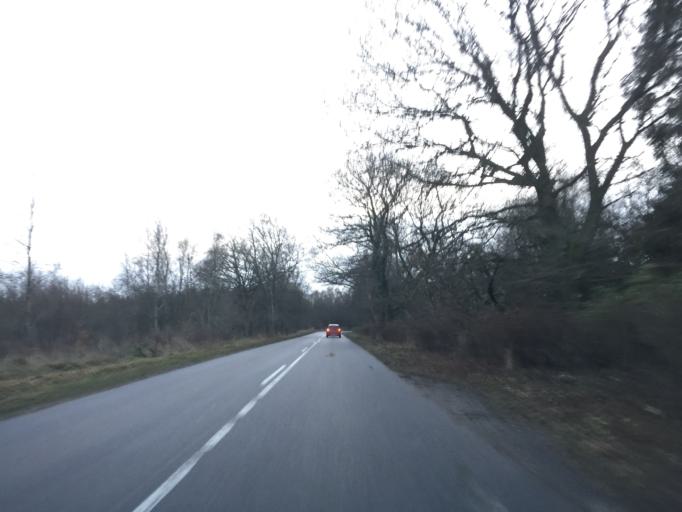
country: DK
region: Central Jutland
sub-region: Viborg Kommune
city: Bjerringbro
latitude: 56.3215
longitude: 9.6240
